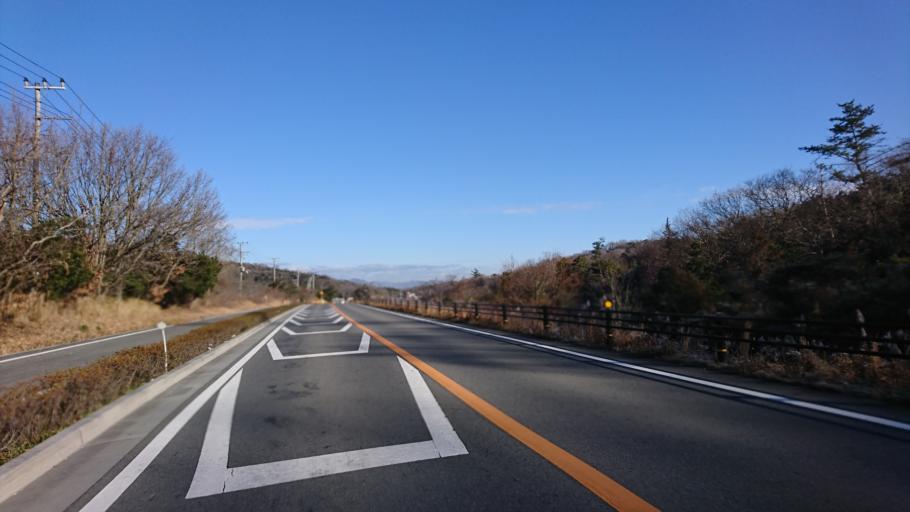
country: JP
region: Hyogo
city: Ono
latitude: 34.8414
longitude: 134.8775
